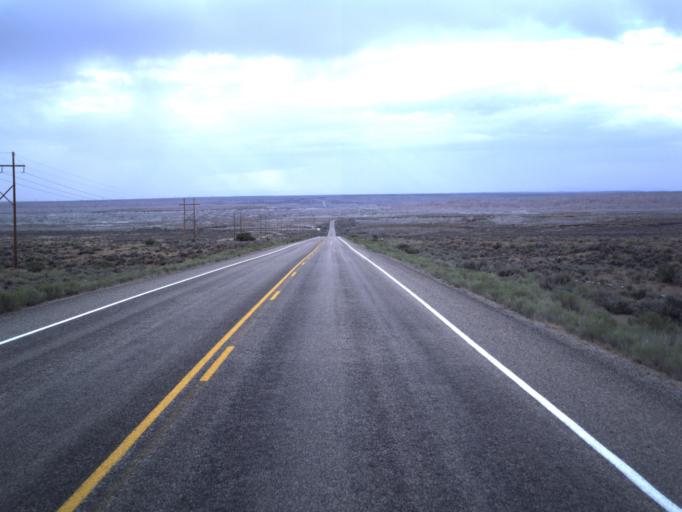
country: US
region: Colorado
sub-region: Rio Blanco County
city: Rangely
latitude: 40.0796
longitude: -109.2118
